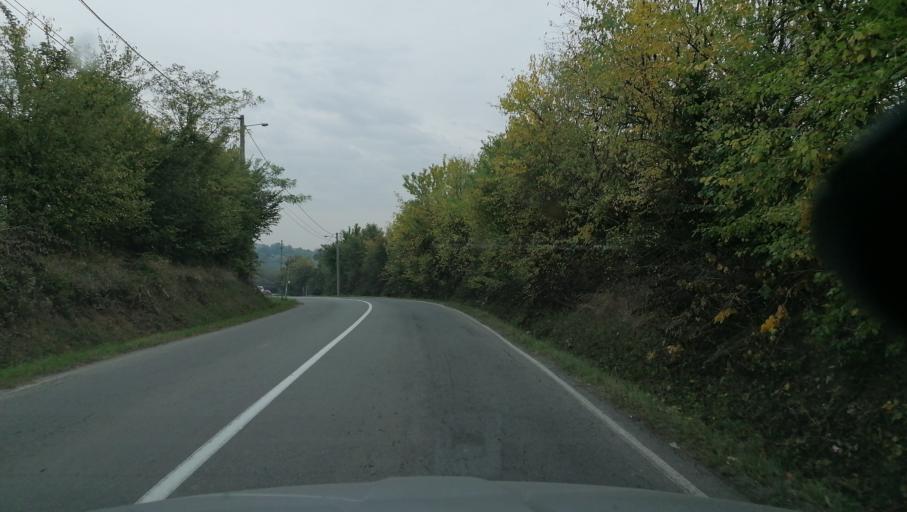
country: RS
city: Rusanj
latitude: 44.6798
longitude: 20.5046
